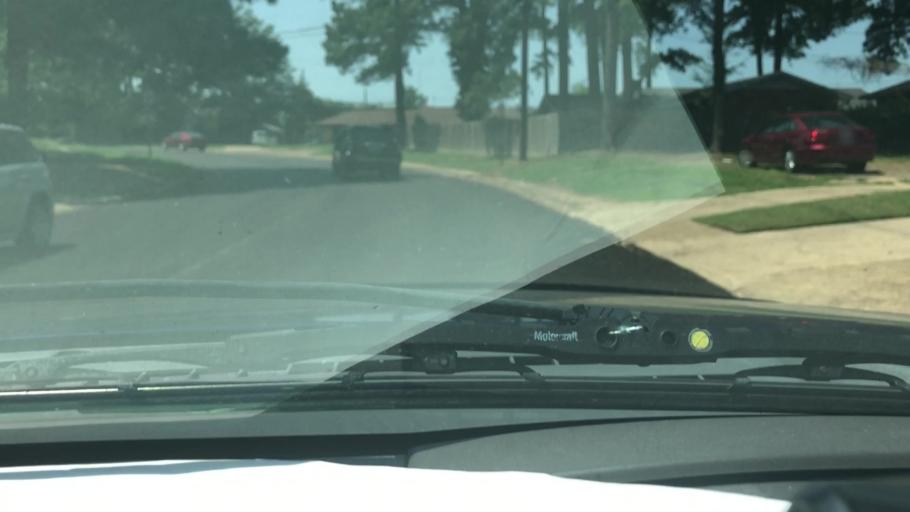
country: US
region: Arkansas
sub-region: Miller County
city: Texarkana
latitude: 33.4557
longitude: -94.0623
